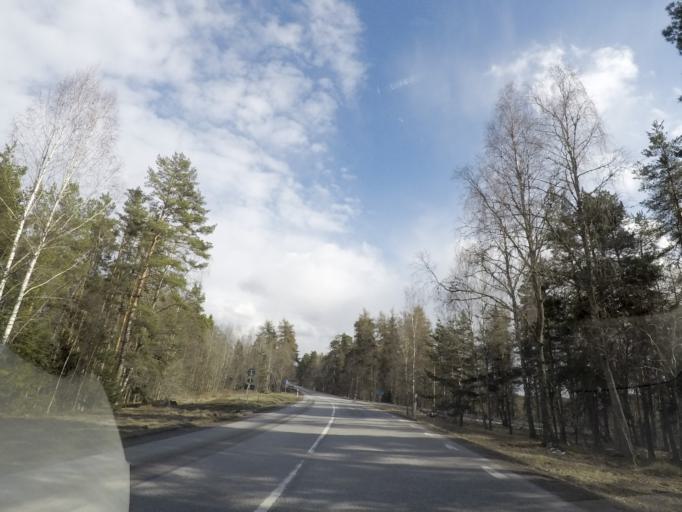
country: SE
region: Vaestmanland
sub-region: Hallstahammars Kommun
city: Hallstahammar
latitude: 59.6570
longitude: 16.1821
